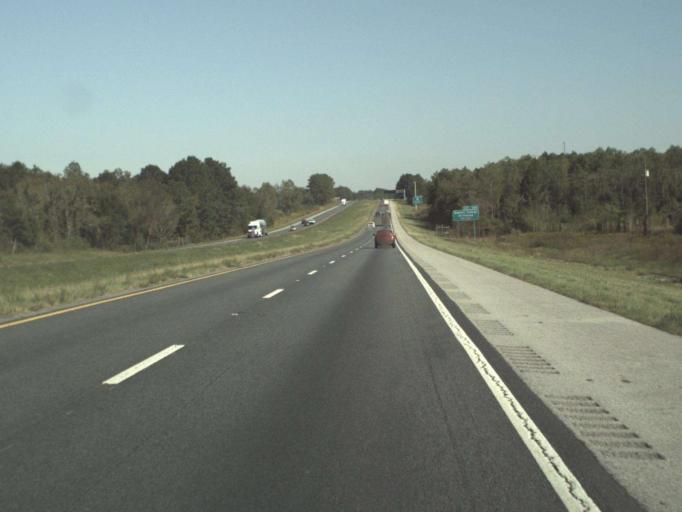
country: US
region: Florida
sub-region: Washington County
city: Chipley
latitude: 30.7515
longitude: -85.5787
